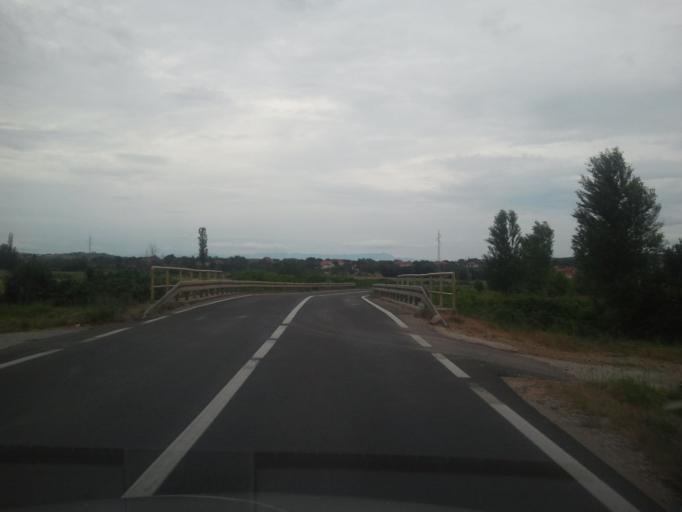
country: HR
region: Zadarska
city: Polaca
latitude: 43.9876
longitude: 15.4868
